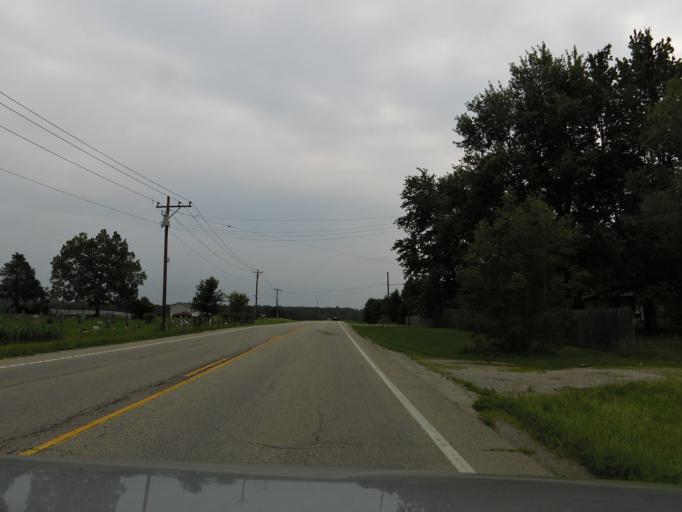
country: US
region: Ohio
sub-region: Brown County
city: Mount Orab
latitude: 38.9759
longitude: -83.9143
